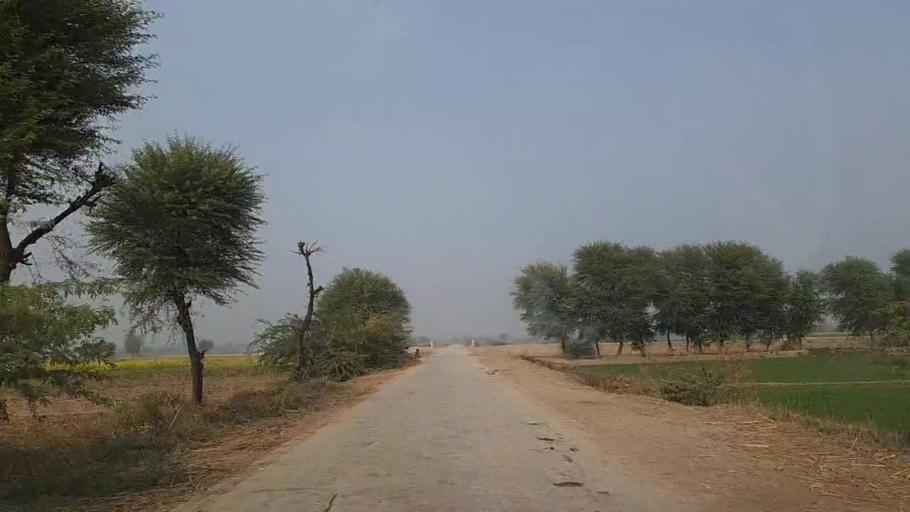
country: PK
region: Sindh
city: Sanghar
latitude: 26.0887
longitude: 68.8974
